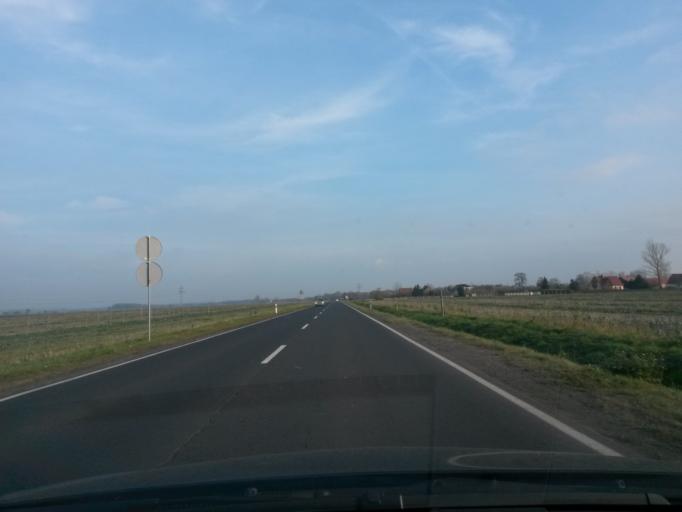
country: PL
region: Lower Silesian Voivodeship
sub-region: Powiat swidnicki
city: Swiebodzice
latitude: 50.9170
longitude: 16.2551
